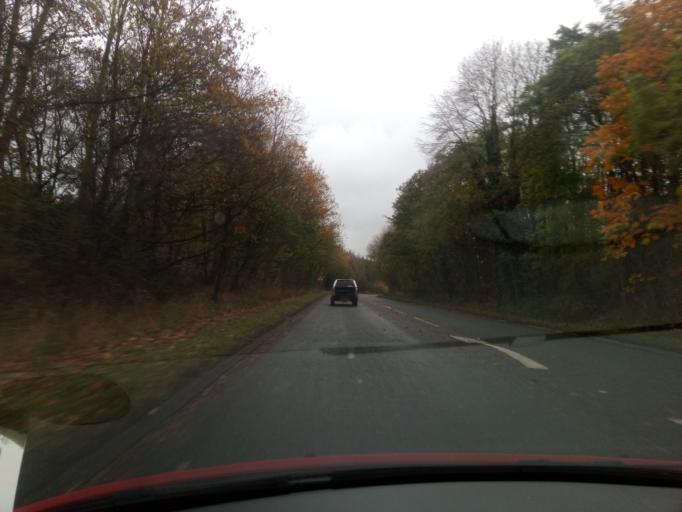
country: GB
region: England
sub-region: County Durham
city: High Etherley
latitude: 54.6688
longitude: -1.7744
